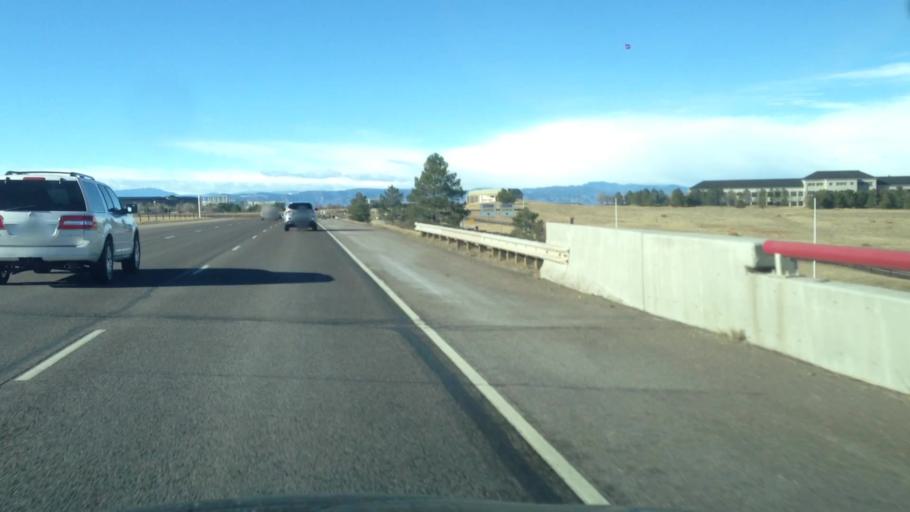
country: US
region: Colorado
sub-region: Douglas County
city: Meridian
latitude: 39.5524
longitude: -104.8397
